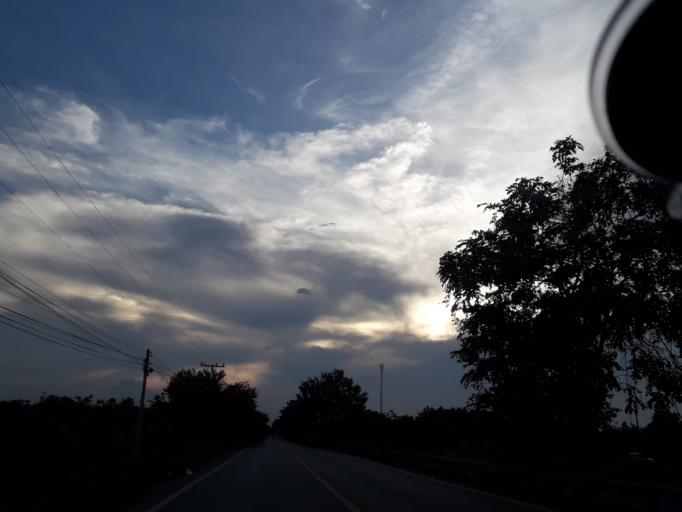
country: TH
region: Sara Buri
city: Nong Khae
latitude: 14.2711
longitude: 100.8815
